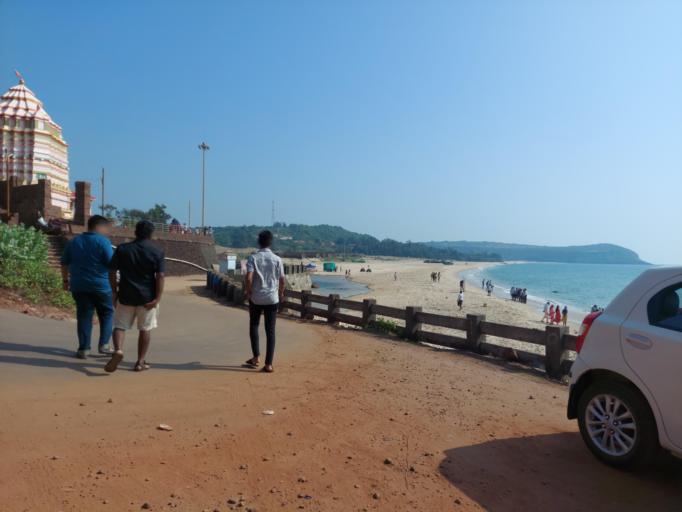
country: IN
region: Maharashtra
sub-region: Sindhudurg
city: Malvan
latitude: 16.3340
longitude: 73.3914
